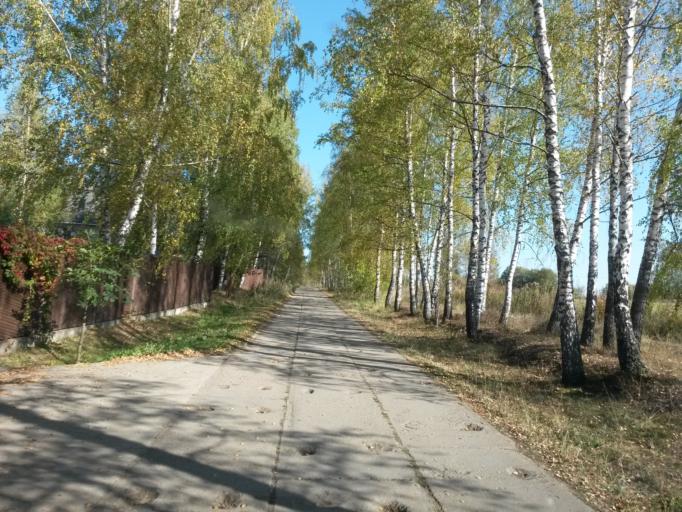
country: RU
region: Moskovskaya
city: Lyubuchany
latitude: 55.2561
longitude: 37.6207
